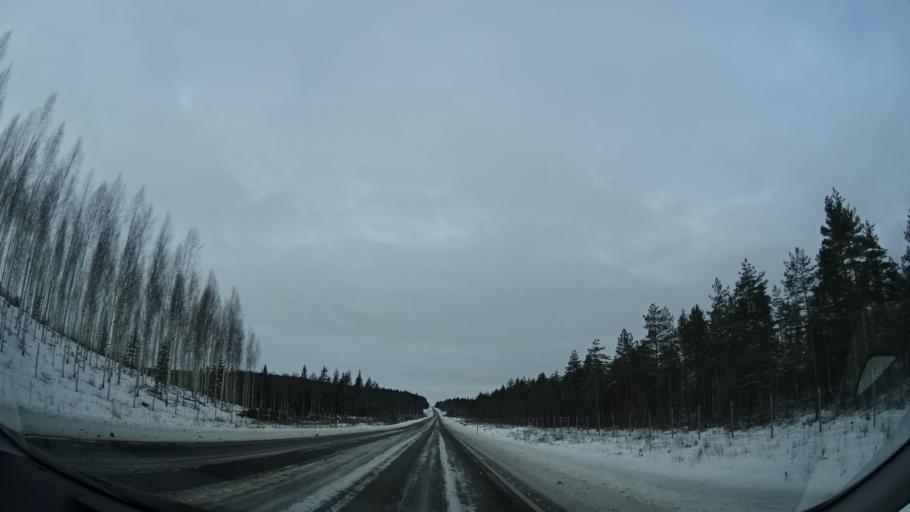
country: FI
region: Uusimaa
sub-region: Helsinki
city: Kaerkoelae
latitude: 60.6214
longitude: 23.9949
